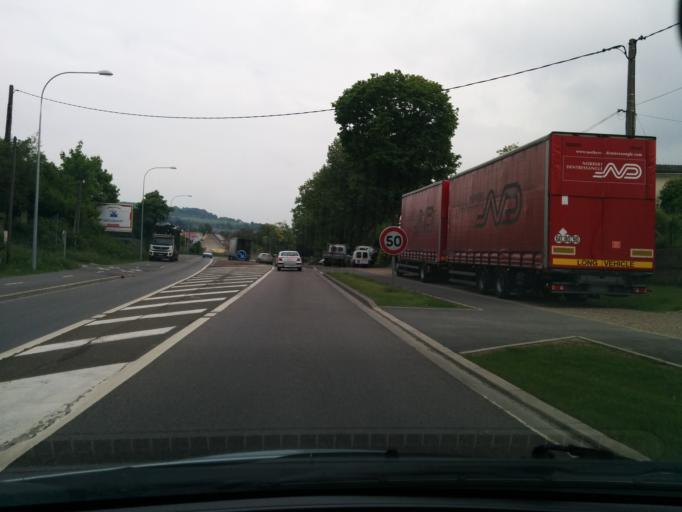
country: FR
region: Ile-de-France
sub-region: Departement des Yvelines
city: Juziers
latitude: 48.9894
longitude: 1.8330
